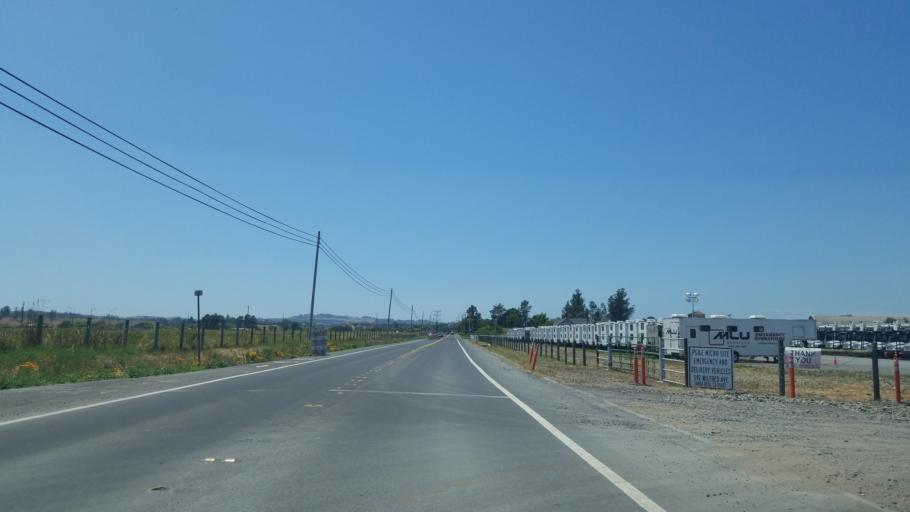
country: US
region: California
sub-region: Sonoma County
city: Rohnert Park
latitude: 38.3633
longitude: -122.7340
